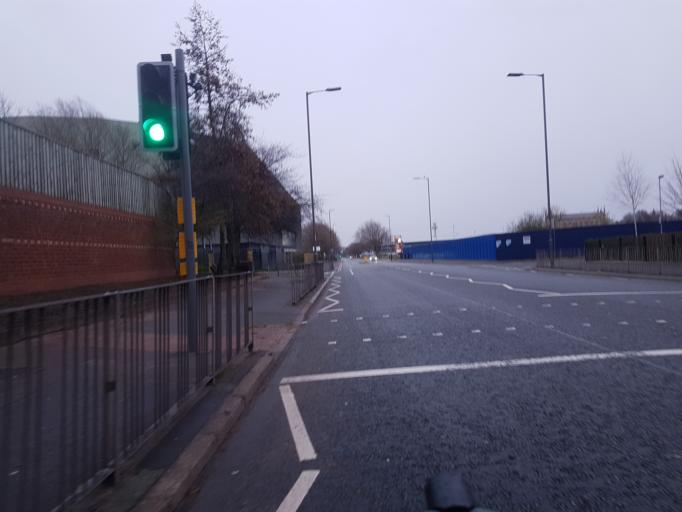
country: GB
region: England
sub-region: Liverpool
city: Liverpool
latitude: 53.4263
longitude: -2.9790
